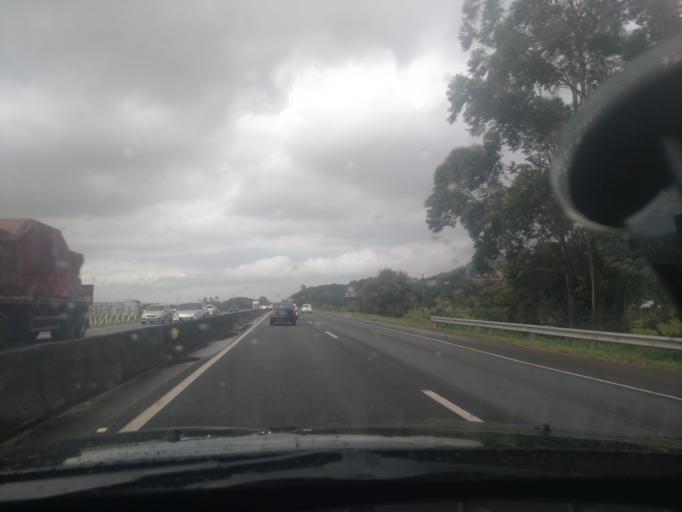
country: BR
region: Santa Catarina
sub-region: Biguacu
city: Biguacu
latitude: -27.4048
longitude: -48.6289
